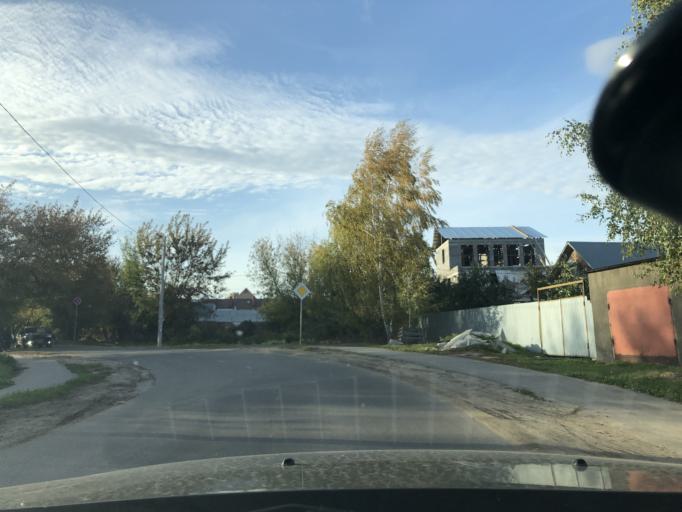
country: RU
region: Tula
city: Tula
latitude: 54.1896
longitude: 37.6329
